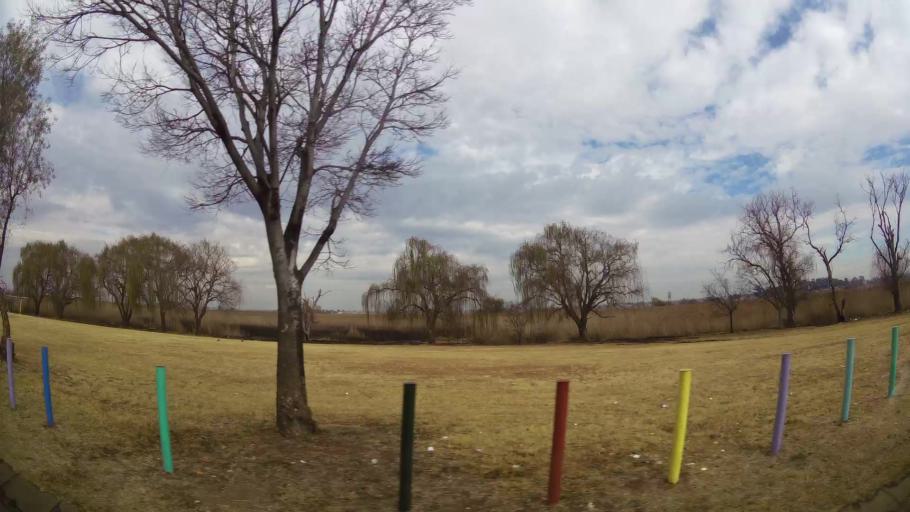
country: ZA
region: Gauteng
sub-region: Ekurhuleni Metropolitan Municipality
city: Germiston
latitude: -26.3302
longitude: 28.1757
